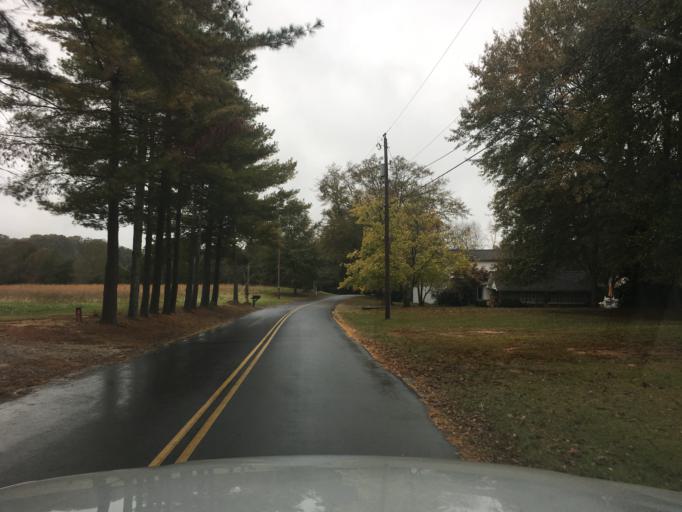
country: US
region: South Carolina
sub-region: Pickens County
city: Central
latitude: 34.7339
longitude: -82.7672
